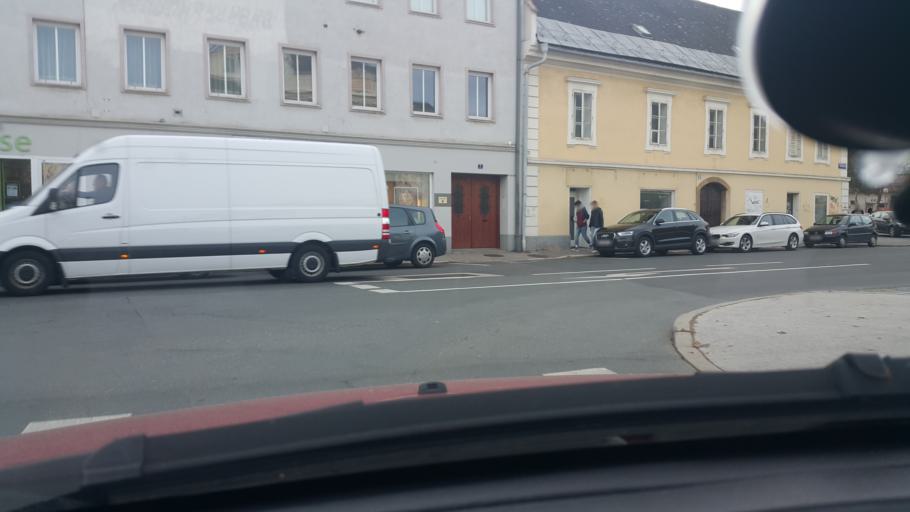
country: AT
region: Carinthia
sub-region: Klagenfurt am Woerthersee
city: Klagenfurt am Woerthersee
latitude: 46.6264
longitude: 14.3048
